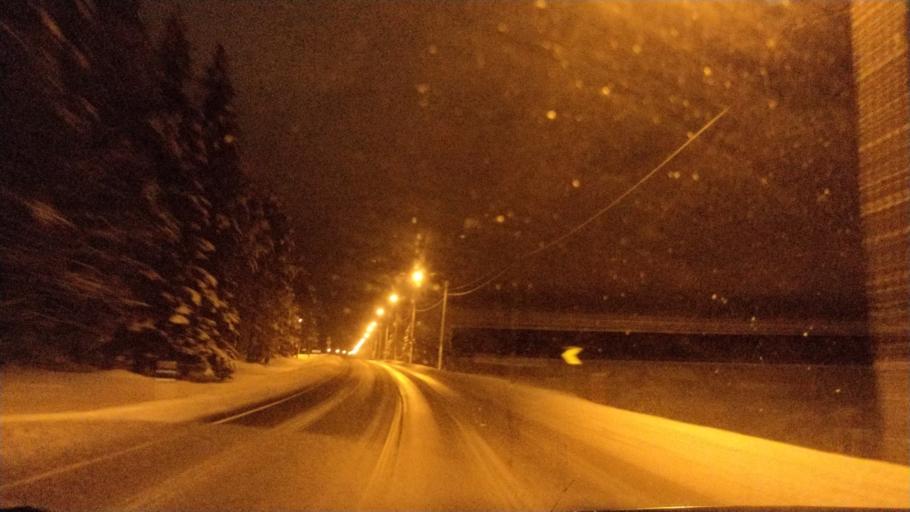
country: FI
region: Lapland
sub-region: Rovaniemi
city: Rovaniemi
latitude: 66.2732
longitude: 25.3296
